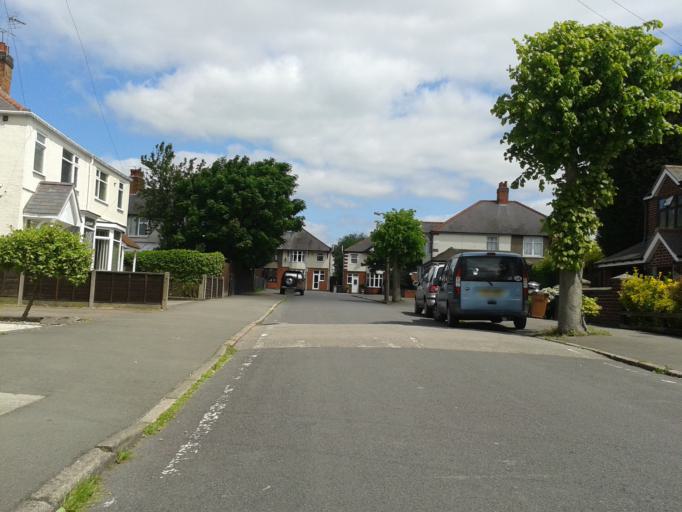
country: GB
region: England
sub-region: Leicestershire
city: Hinckley
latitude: 52.5426
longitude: -1.3560
